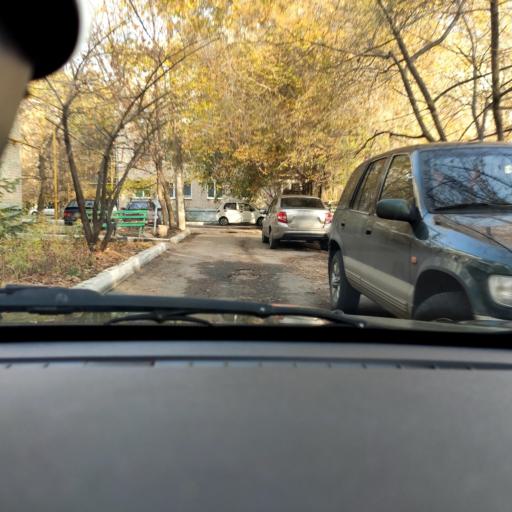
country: RU
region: Samara
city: Tol'yatti
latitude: 53.5141
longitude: 49.4157
